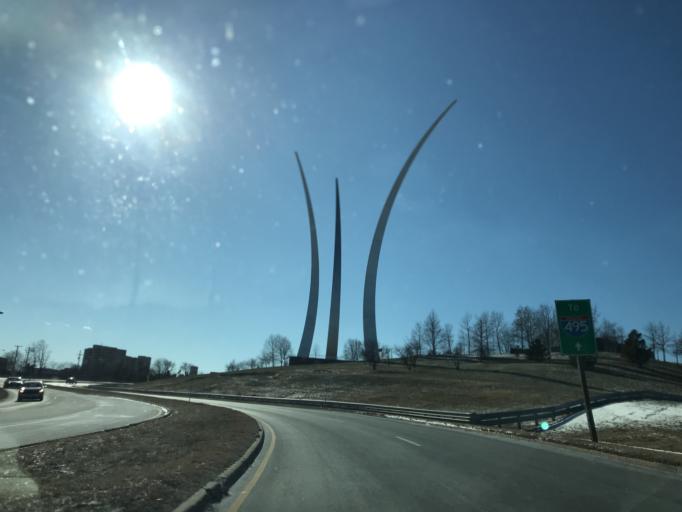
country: US
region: Washington, D.C.
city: Washington, D.C.
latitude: 38.8701
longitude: -77.0658
